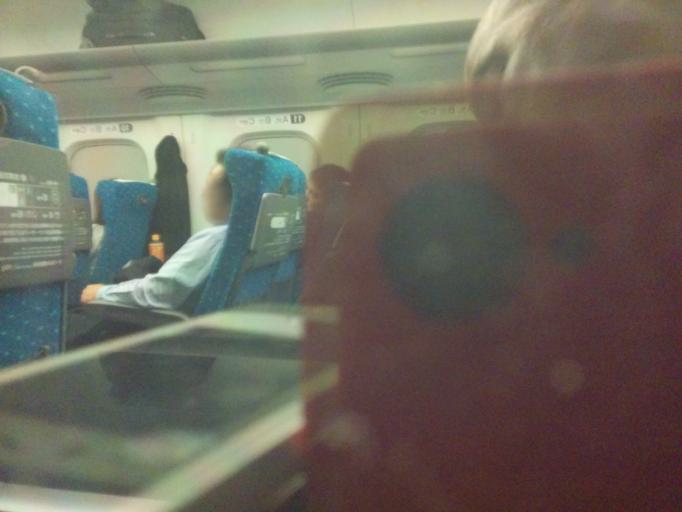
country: JP
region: Shizuoka
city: Shizuoka-shi
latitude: 35.0673
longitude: 138.5176
